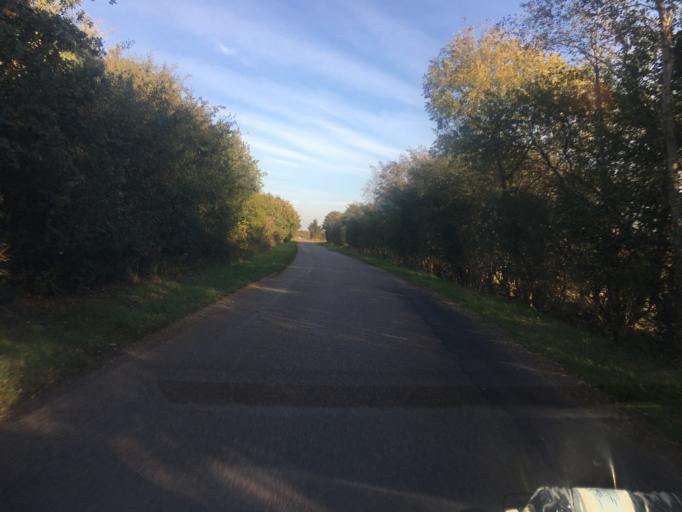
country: DE
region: Schleswig-Holstein
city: Ellhoft
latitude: 54.9135
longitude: 8.9188
